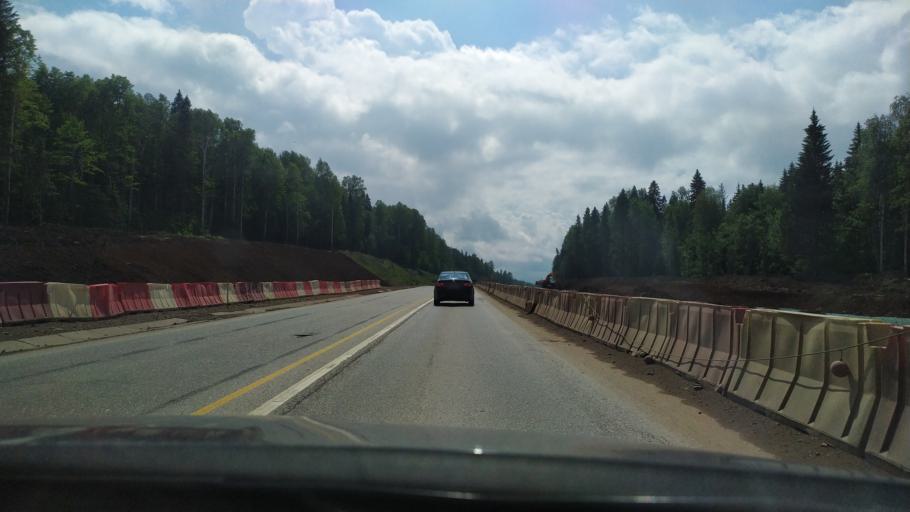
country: RU
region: Perm
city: Novyye Lyady
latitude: 58.0843
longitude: 56.4298
